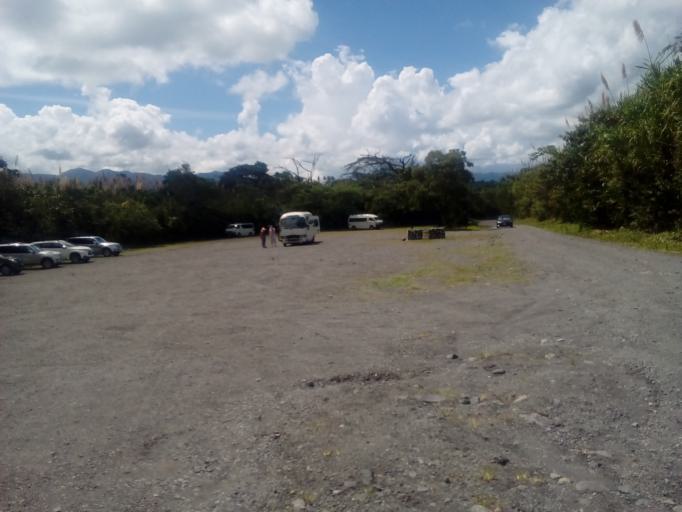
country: CR
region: Alajuela
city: La Fortuna
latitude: 10.4604
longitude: -84.7354
